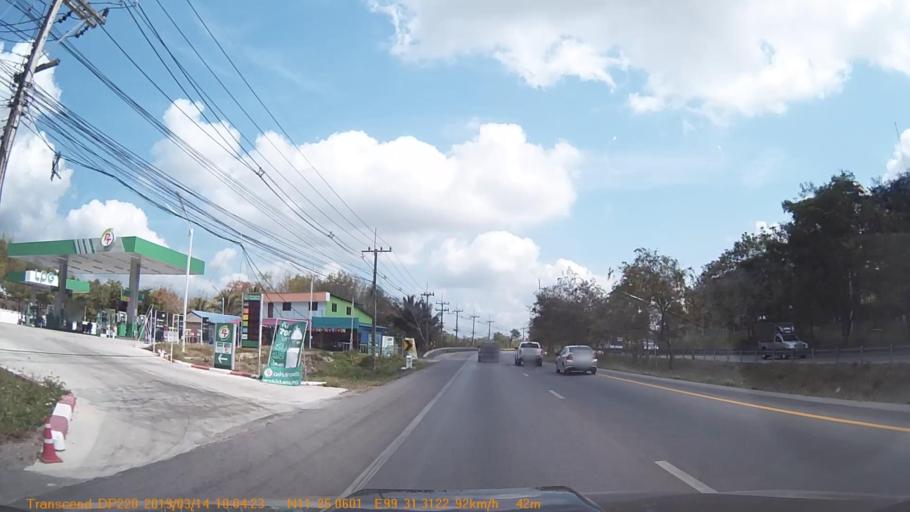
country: TH
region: Prachuap Khiri Khan
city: Thap Sakae
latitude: 11.4182
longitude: 99.5219
